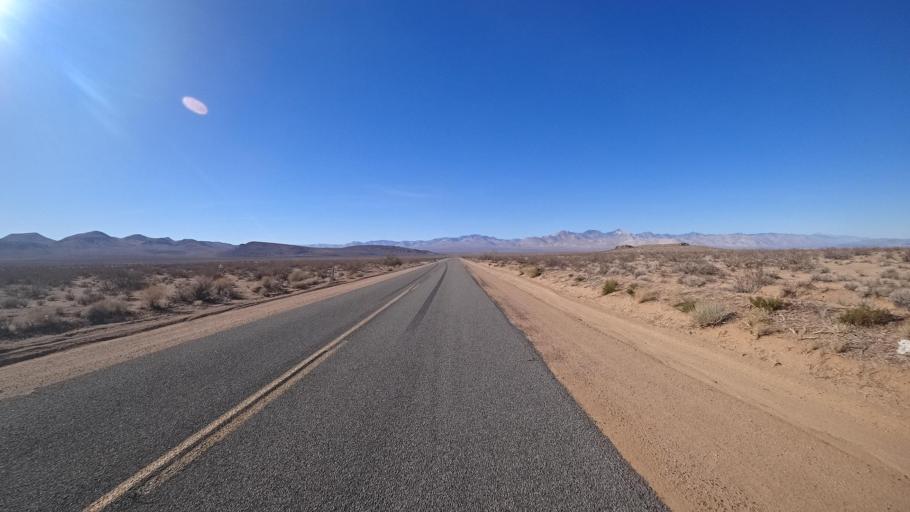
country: US
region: California
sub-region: Kern County
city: Ridgecrest
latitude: 35.5504
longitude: -117.7183
